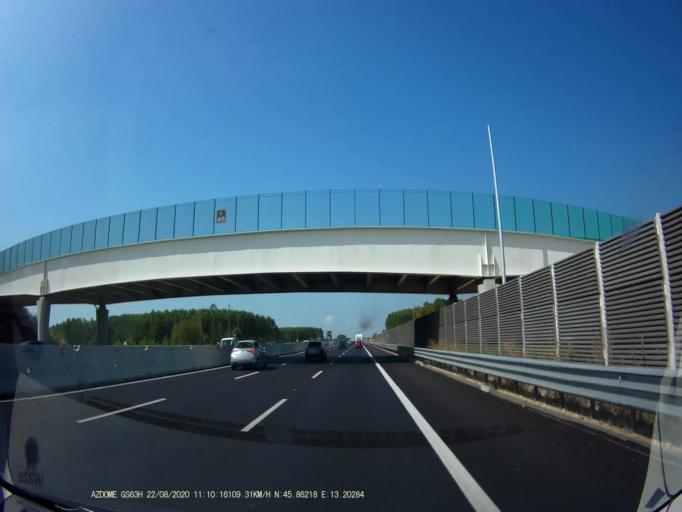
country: IT
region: Friuli Venezia Giulia
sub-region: Provincia di Udine
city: Porpetto
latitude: 45.8614
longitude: 13.2026
